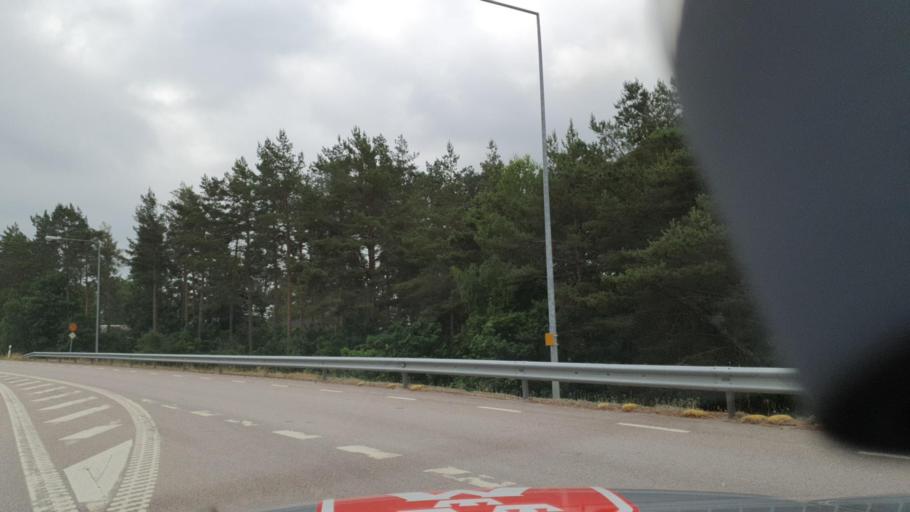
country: SE
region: Kalmar
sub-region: Kalmar Kommun
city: Ljungbyholm
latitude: 56.5930
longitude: 16.1262
